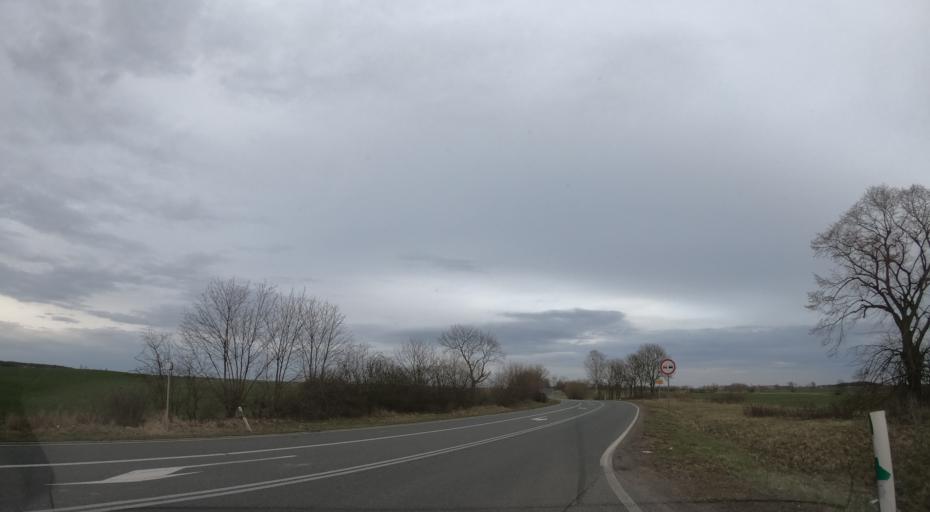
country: PL
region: West Pomeranian Voivodeship
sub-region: Powiat mysliborski
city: Nowogrodek Pomorski
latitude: 52.9038
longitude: 14.9760
